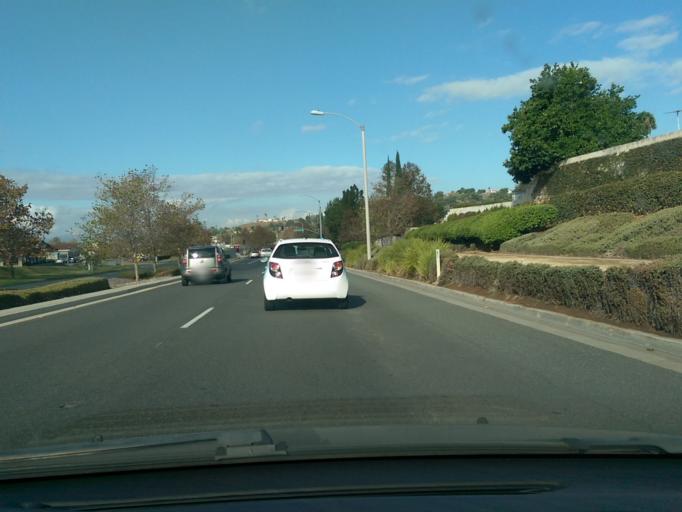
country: US
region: California
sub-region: Riverside County
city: Pedley
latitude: 33.9787
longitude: -117.4526
